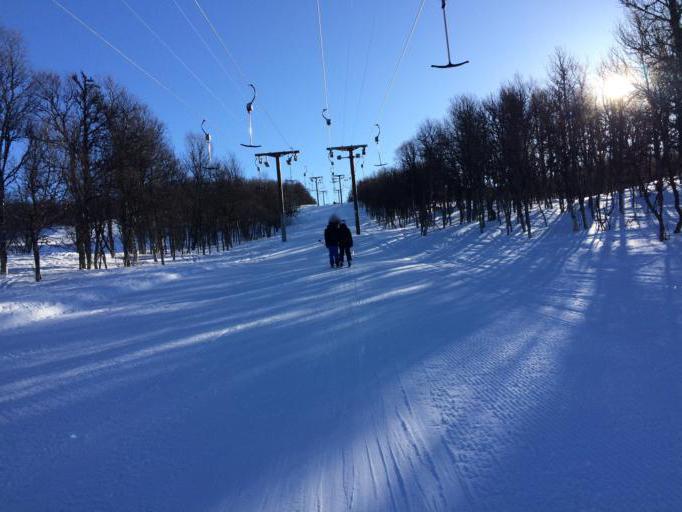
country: SE
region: Jaemtland
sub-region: Are Kommun
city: Are
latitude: 63.4302
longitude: 13.0227
